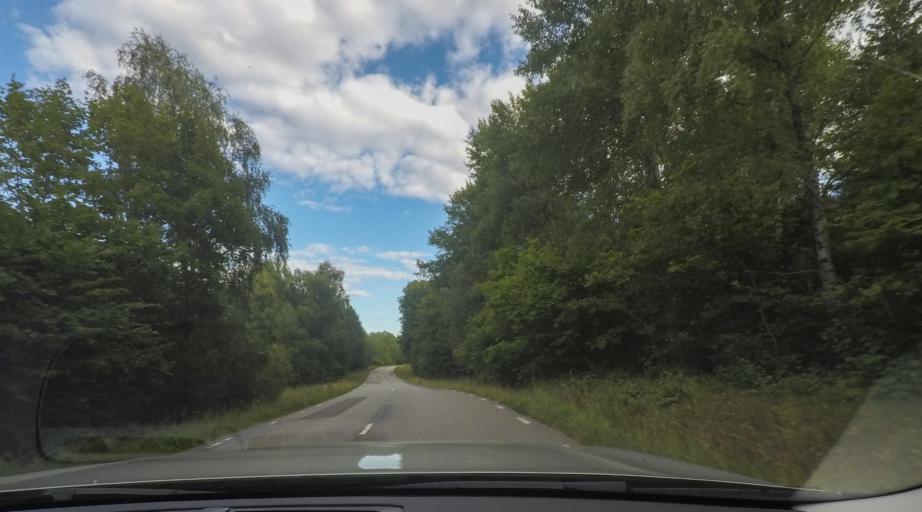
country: SE
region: Soedermanland
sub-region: Trosa Kommun
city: Trosa
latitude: 58.9807
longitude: 17.6881
